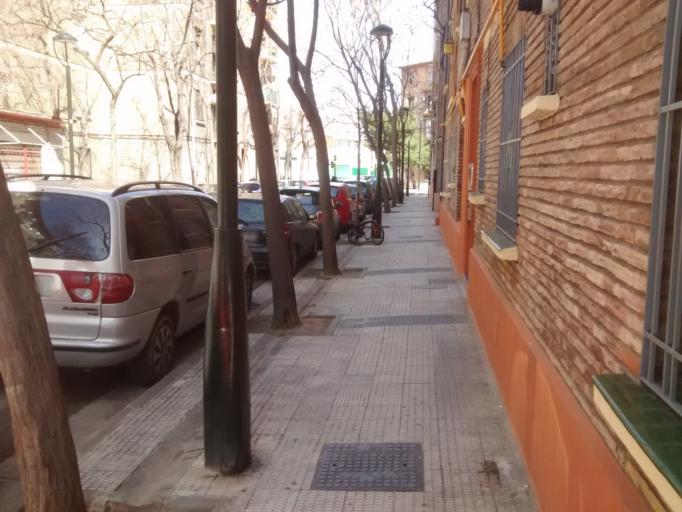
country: ES
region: Aragon
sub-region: Provincia de Zaragoza
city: Zaragoza
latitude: 41.6451
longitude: -0.8679
